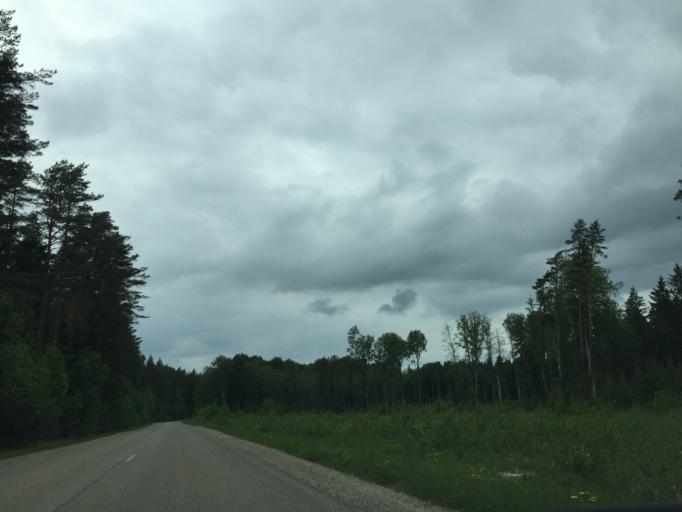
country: LV
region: Varkava
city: Vecvarkava
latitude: 56.0745
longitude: 26.6340
